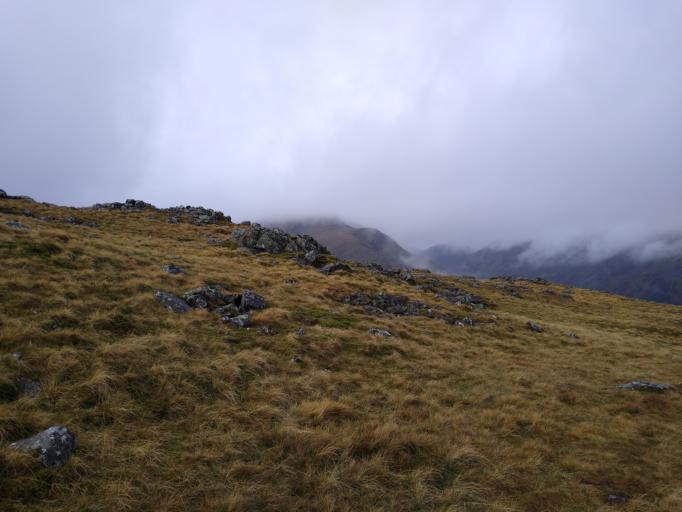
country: GB
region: England
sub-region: Cumbria
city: Keswick
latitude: 54.4874
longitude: -3.2467
